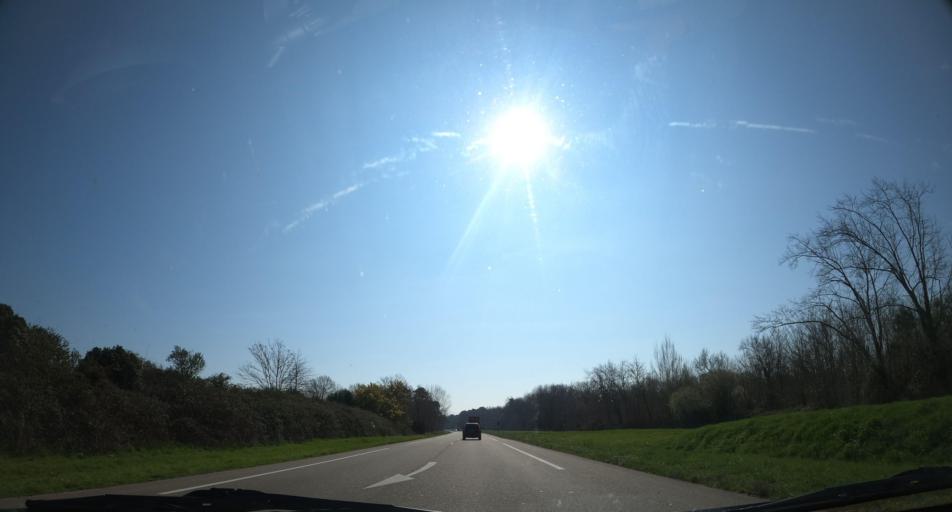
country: FR
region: Aquitaine
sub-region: Departement des Landes
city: Saint-Pierre-du-Mont
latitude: 43.8755
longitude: -0.5215
